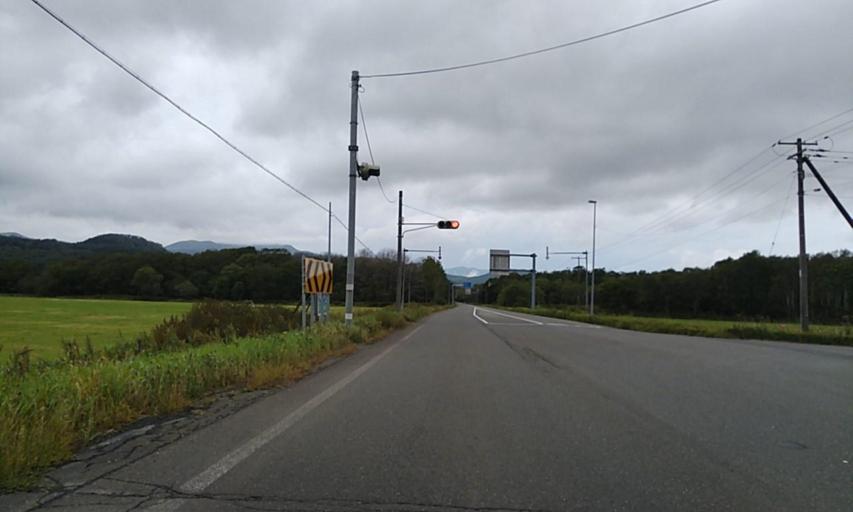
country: JP
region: Hokkaido
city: Bihoro
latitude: 43.5160
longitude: 144.4306
